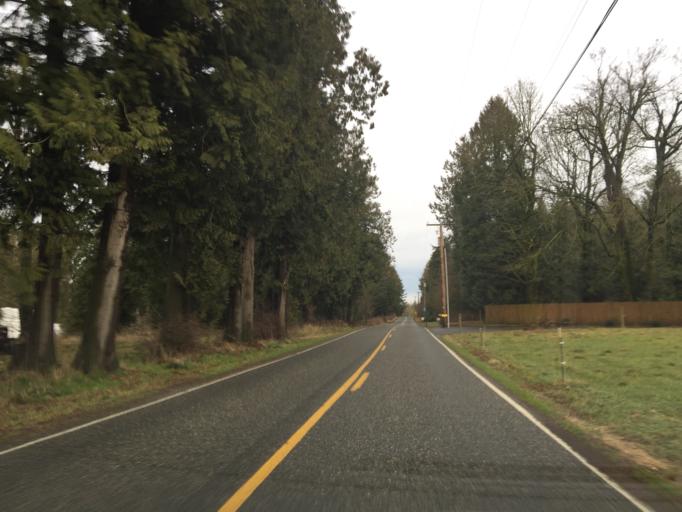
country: US
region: Washington
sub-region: Whatcom County
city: Ferndale
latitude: 48.8963
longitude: -122.5387
